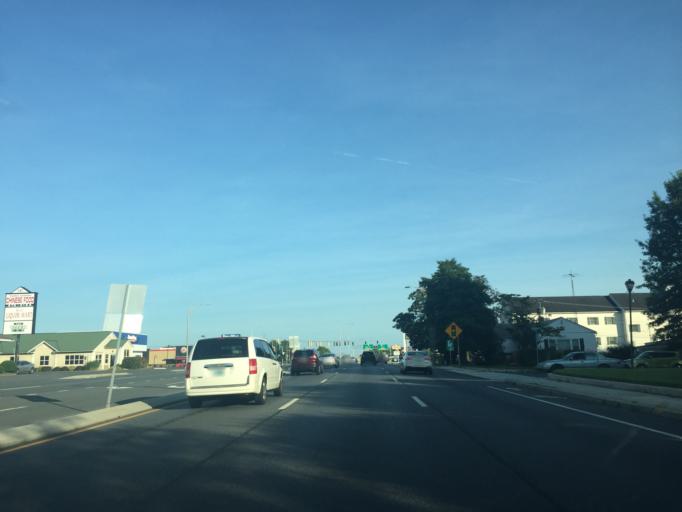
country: US
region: Delaware
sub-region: Kent County
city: Dover
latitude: 39.1628
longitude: -75.5149
